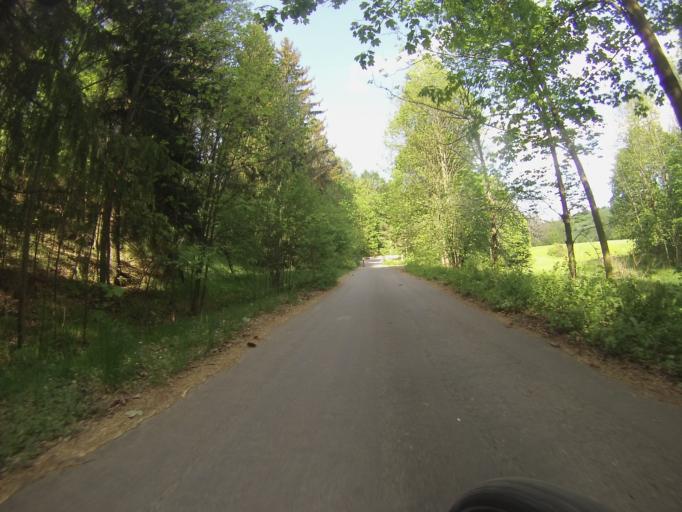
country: CZ
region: South Moravian
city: Ostrov u Macochy
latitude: 49.3693
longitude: 16.7376
